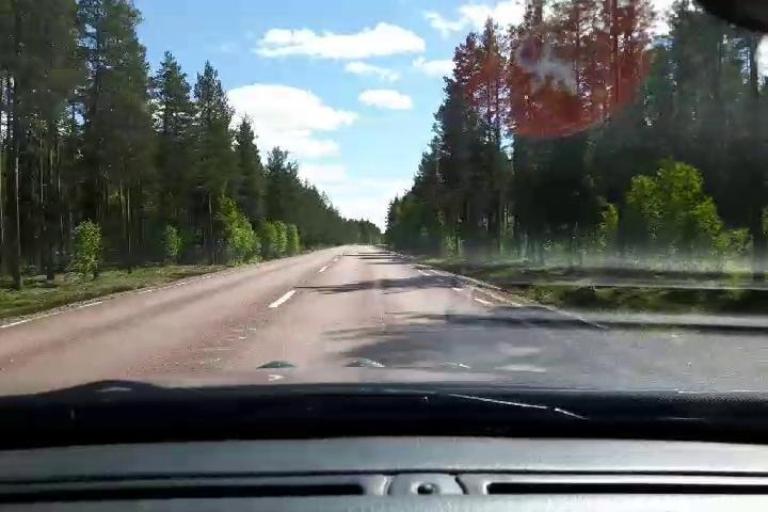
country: SE
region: Gaevleborg
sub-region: Ljusdals Kommun
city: Farila
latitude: 61.8273
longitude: 15.7539
